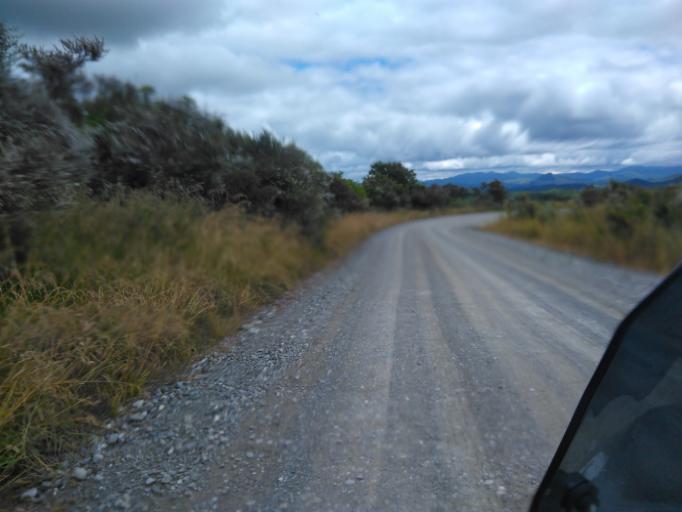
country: NZ
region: Gisborne
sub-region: Gisborne District
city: Gisborne
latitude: -38.1633
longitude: 178.1351
